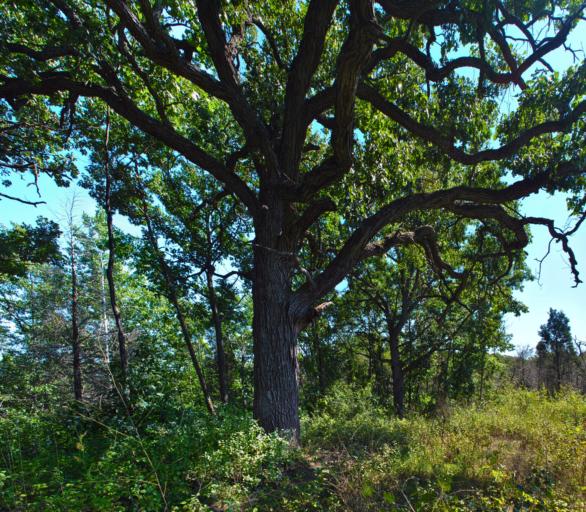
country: US
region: Wisconsin
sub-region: Walworth County
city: East Troy
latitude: 42.8185
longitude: -88.4106
